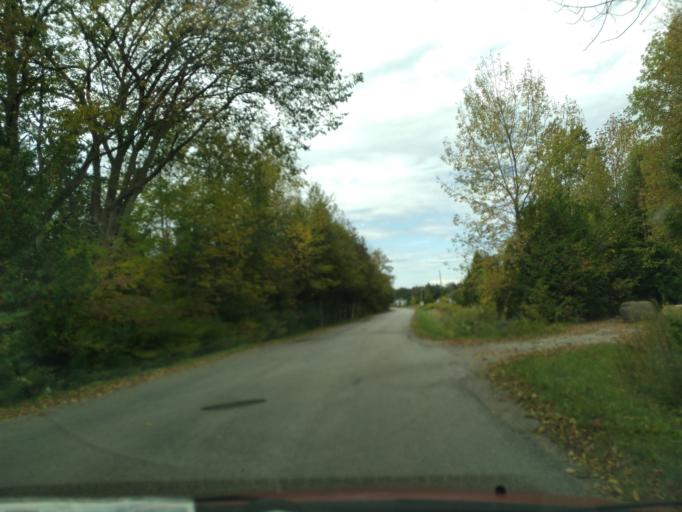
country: CA
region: Ontario
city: Keswick
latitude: 44.2613
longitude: -79.3533
